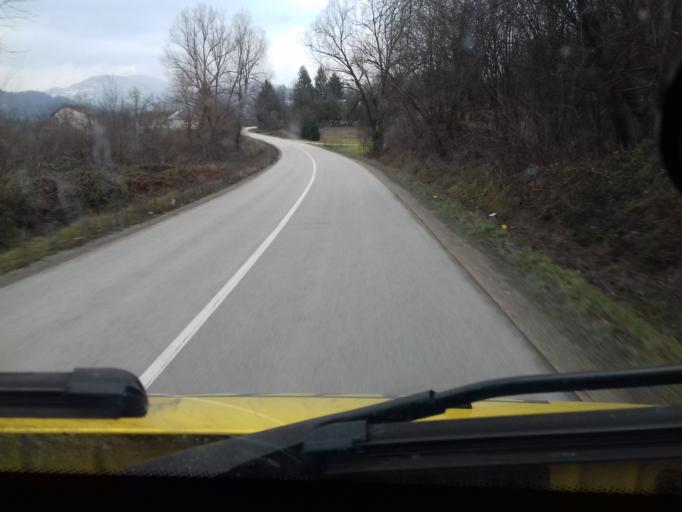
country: BA
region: Federation of Bosnia and Herzegovina
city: Dubravica
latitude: 44.4201
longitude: 18.0920
